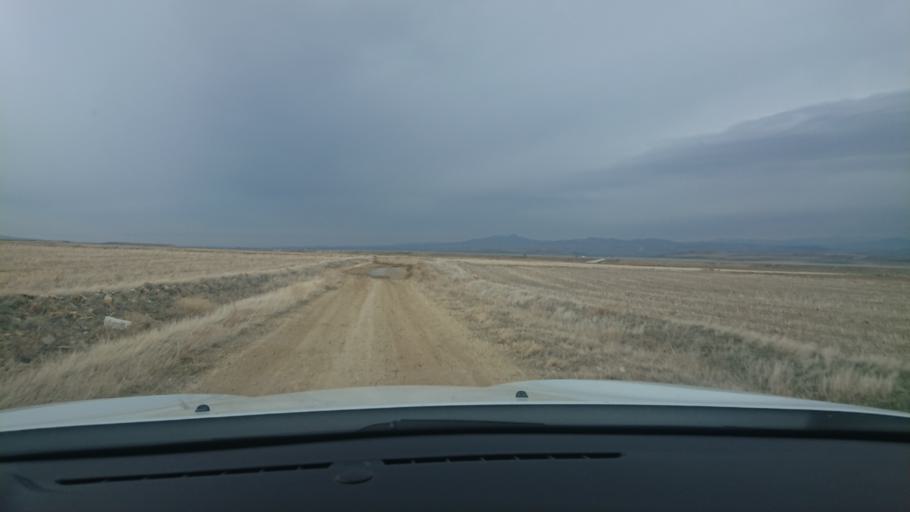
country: TR
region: Aksaray
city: Sariyahsi
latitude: 38.9813
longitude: 33.8783
